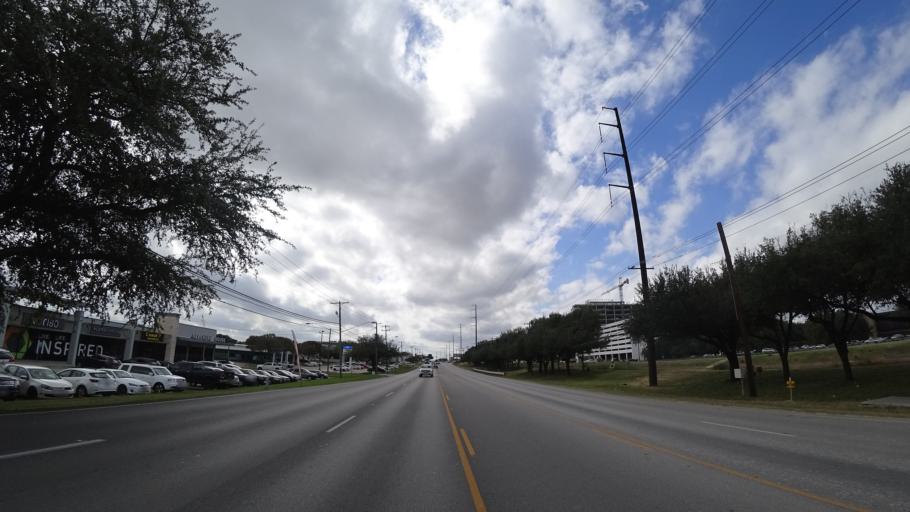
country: US
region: Texas
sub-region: Travis County
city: Wells Branch
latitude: 30.3946
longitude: -97.7206
